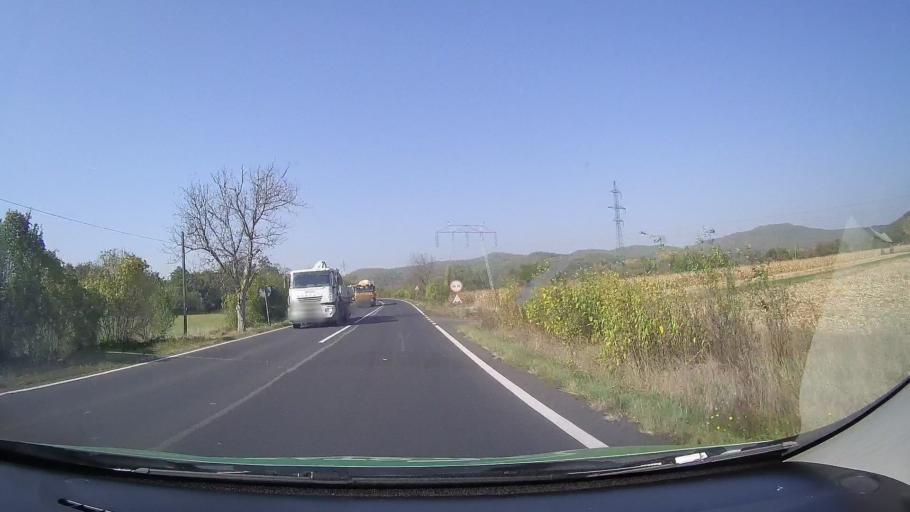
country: RO
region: Hunedoara
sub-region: Comuna Dobra
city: Dobra
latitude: 45.9470
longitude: 22.5985
